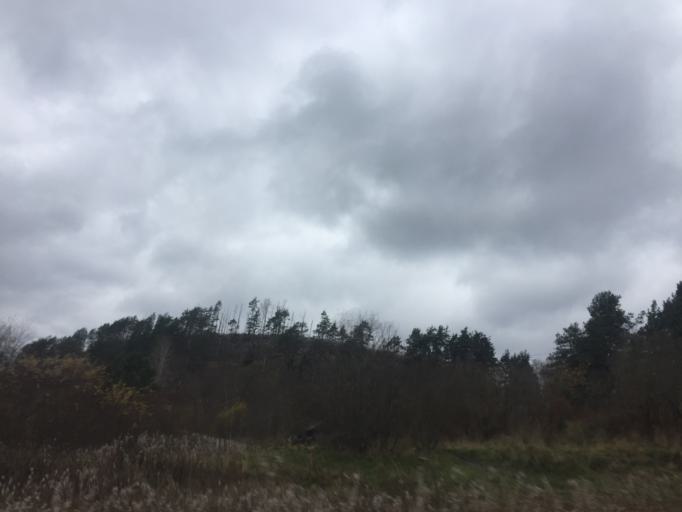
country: RU
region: Republic of Karelia
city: Lakhdenpokh'ya
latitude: 61.4401
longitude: 30.1489
